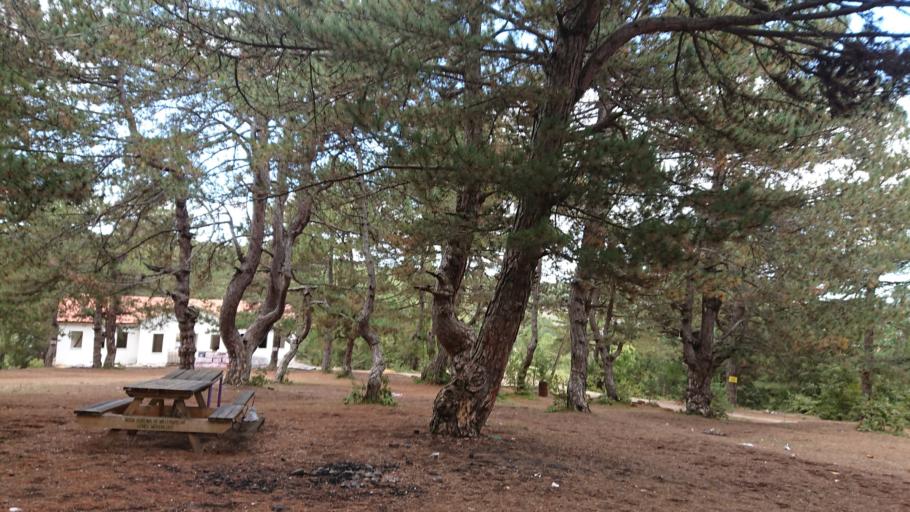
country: TR
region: Bilecik
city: Pazaryeri
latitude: 40.0142
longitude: 29.7970
